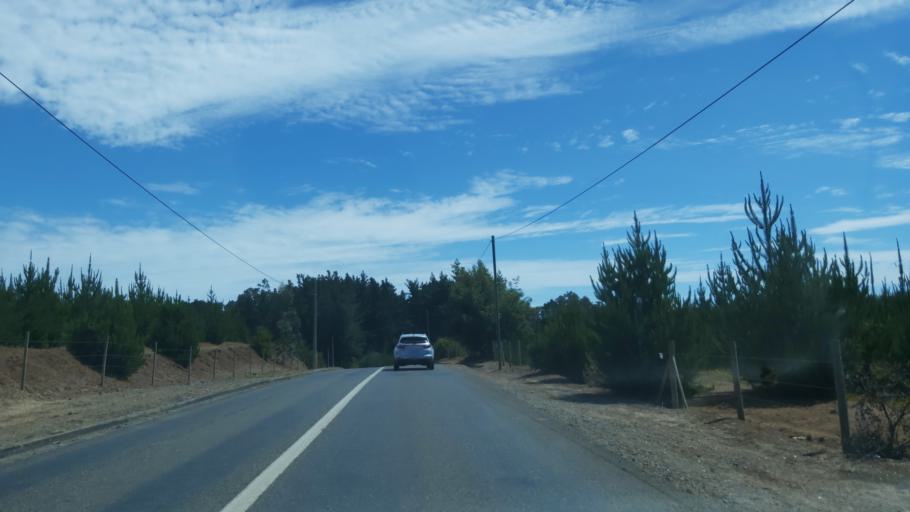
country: CL
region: Maule
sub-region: Provincia de Talca
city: Constitucion
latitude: -35.5118
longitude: -72.5265
